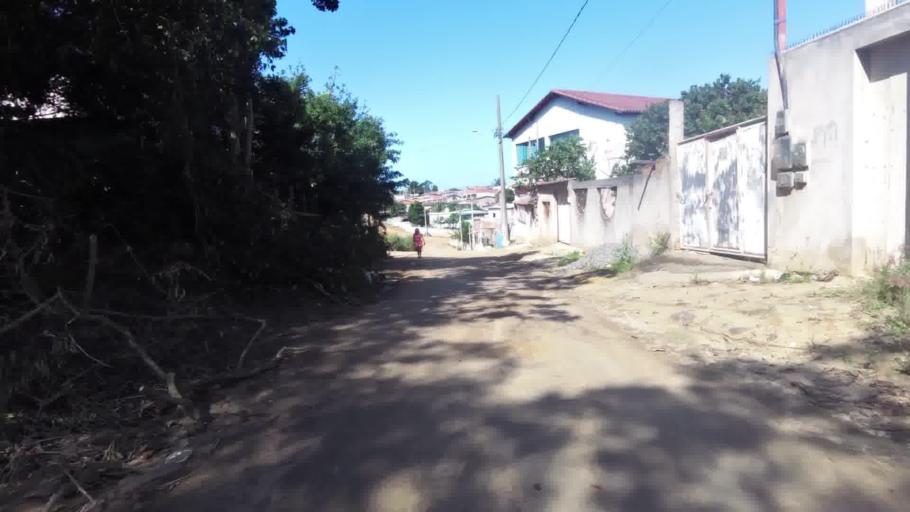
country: BR
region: Espirito Santo
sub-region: Piuma
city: Piuma
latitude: -20.8194
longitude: -40.6260
